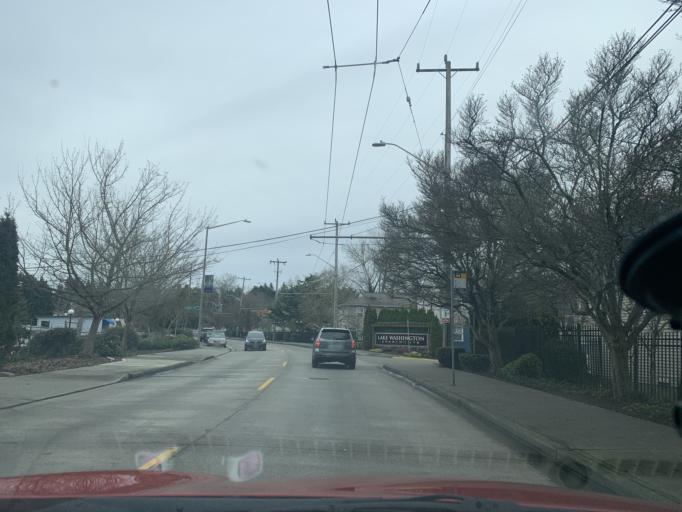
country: US
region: Washington
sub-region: King County
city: Bryn Mawr-Skyway
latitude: 47.5218
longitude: -122.2644
